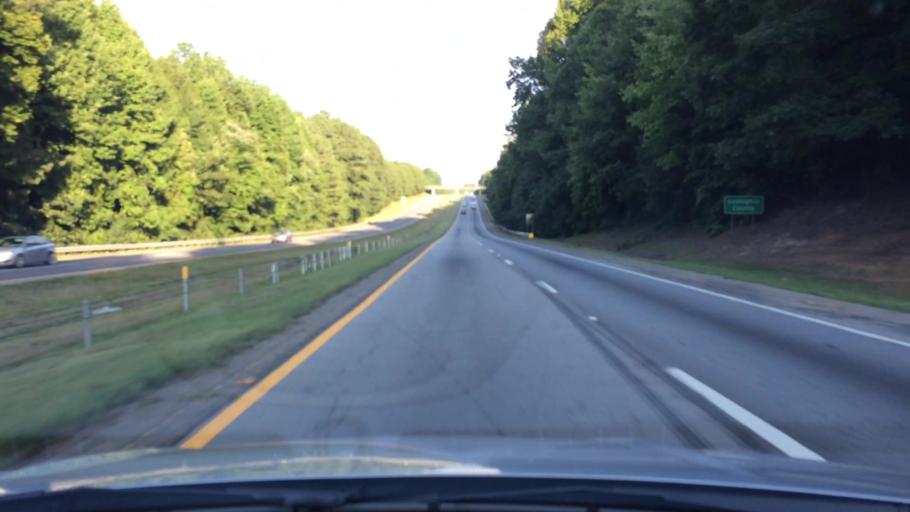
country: US
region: South Carolina
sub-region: Lexington County
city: Chapin
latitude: 34.1954
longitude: -81.3547
